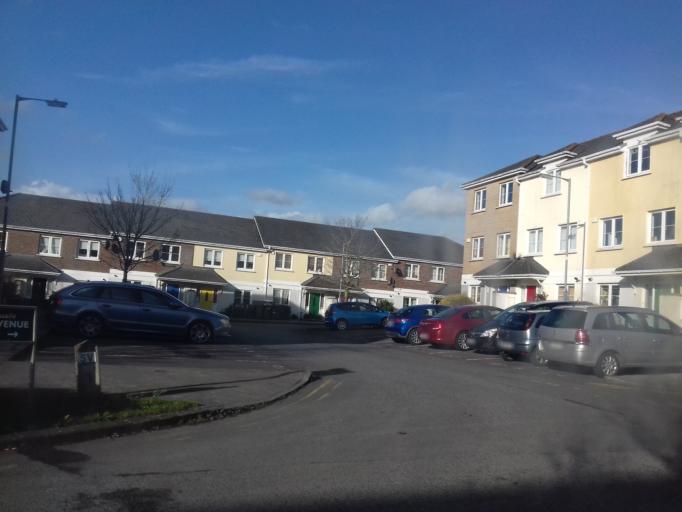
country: IE
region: Leinster
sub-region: Fingal County
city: Blanchardstown
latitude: 53.4184
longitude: -6.3876
